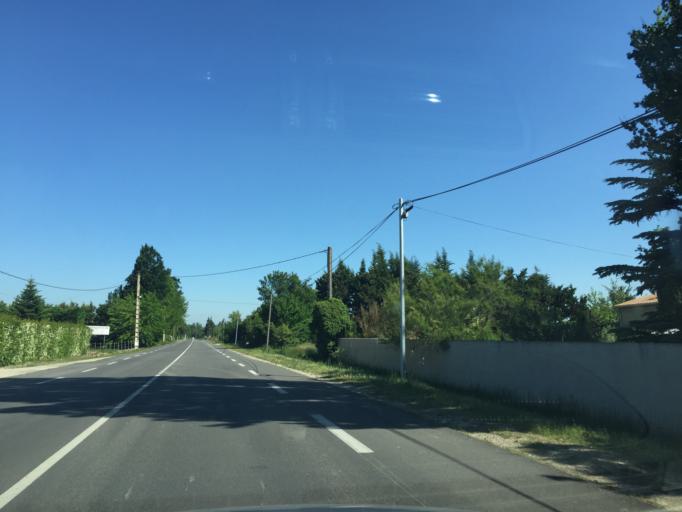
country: FR
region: Provence-Alpes-Cote d'Azur
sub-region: Departement du Vaucluse
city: Monteux
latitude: 44.0091
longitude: 5.0114
